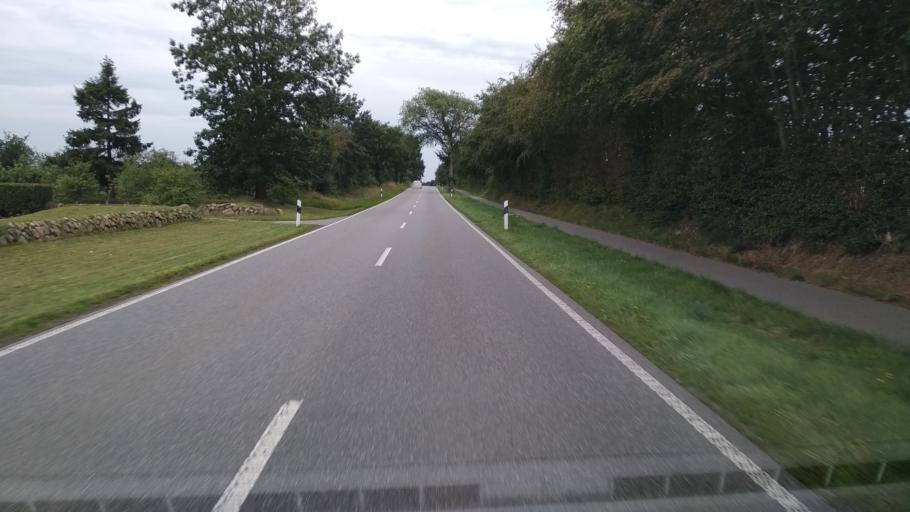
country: DE
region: Schleswig-Holstein
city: Lurschau
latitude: 54.5351
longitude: 9.4921
